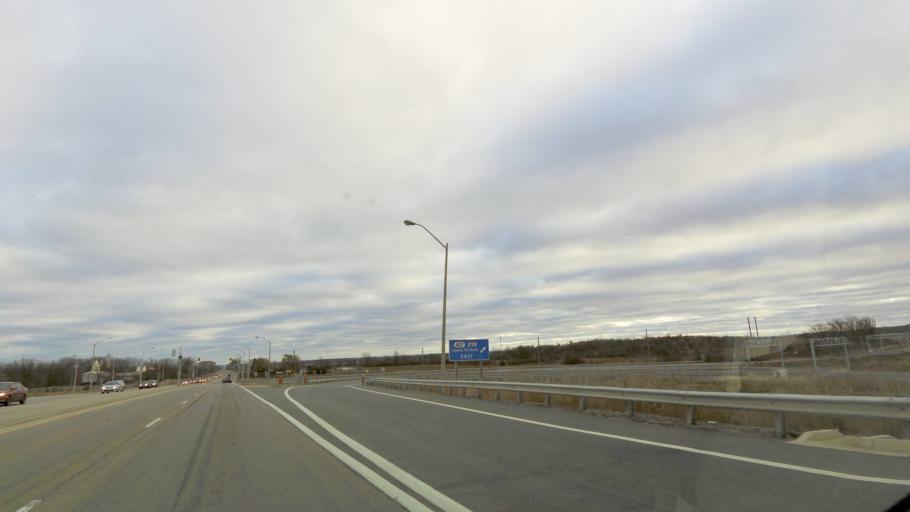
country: CA
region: Ontario
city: Burlington
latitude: 43.4449
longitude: -79.7894
